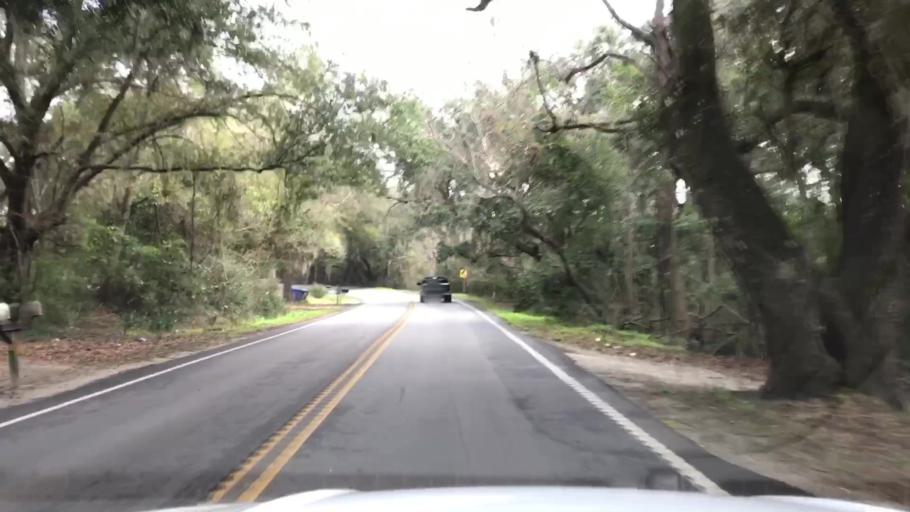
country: US
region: South Carolina
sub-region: Charleston County
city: Kiawah Island
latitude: 32.6780
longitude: -80.0352
